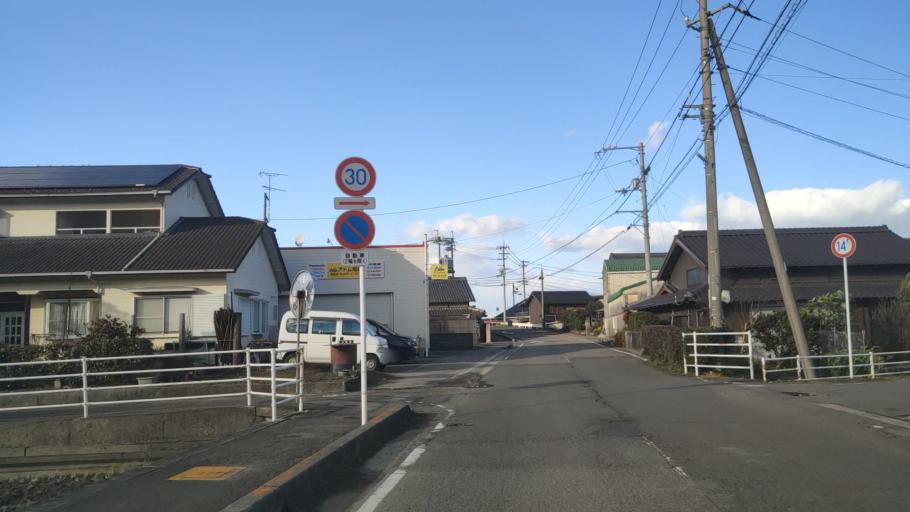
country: JP
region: Ehime
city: Saijo
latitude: 33.9061
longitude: 133.1292
